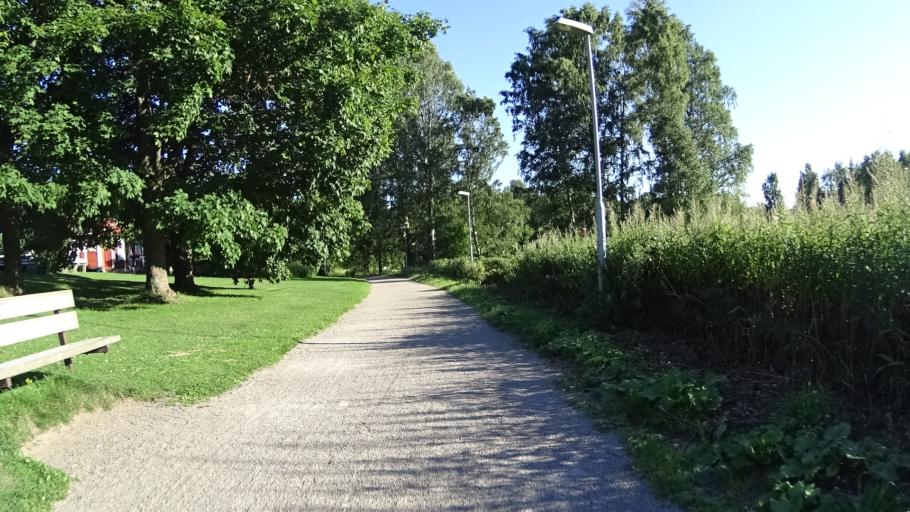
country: FI
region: Uusimaa
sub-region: Helsinki
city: Teekkarikylae
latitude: 60.2154
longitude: 24.8583
